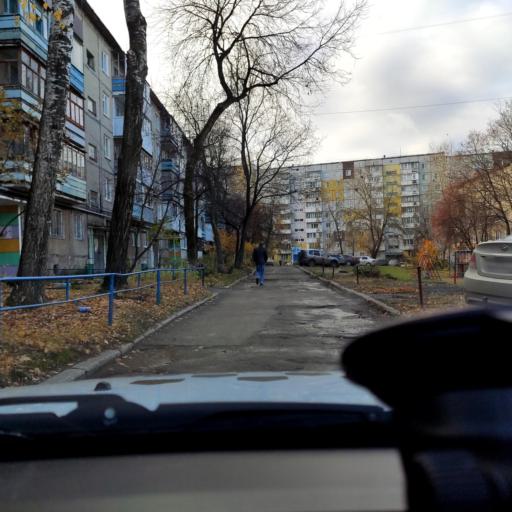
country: RU
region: Perm
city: Kondratovo
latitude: 57.9665
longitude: 56.1668
